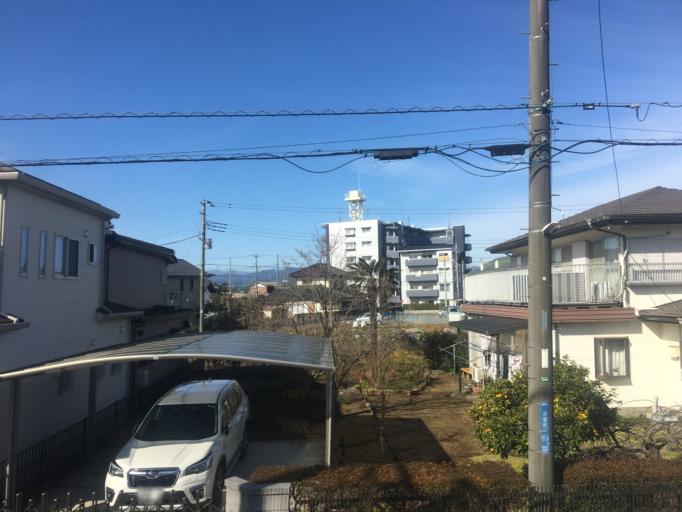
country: JP
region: Saitama
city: Sakado
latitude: 35.9603
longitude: 139.3889
